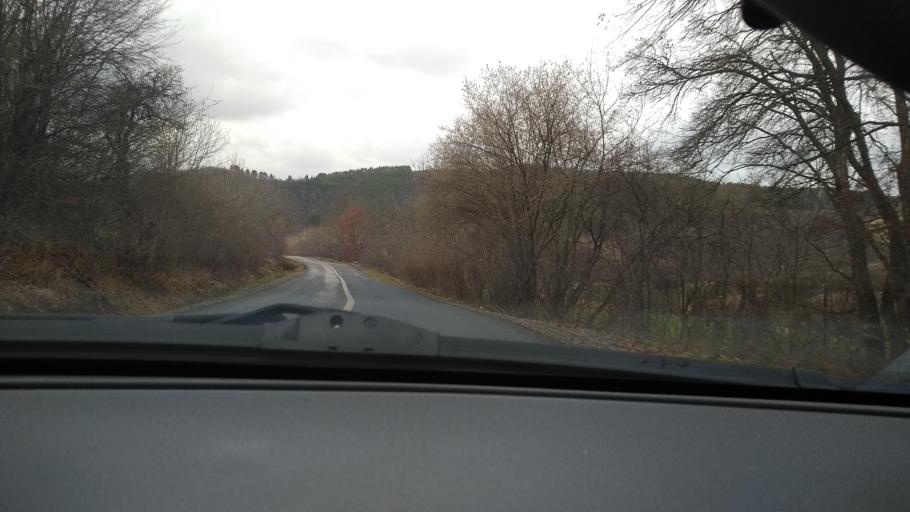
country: RO
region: Mures
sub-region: Comuna Pasareni
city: Pasareni
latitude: 46.5347
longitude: 24.6997
